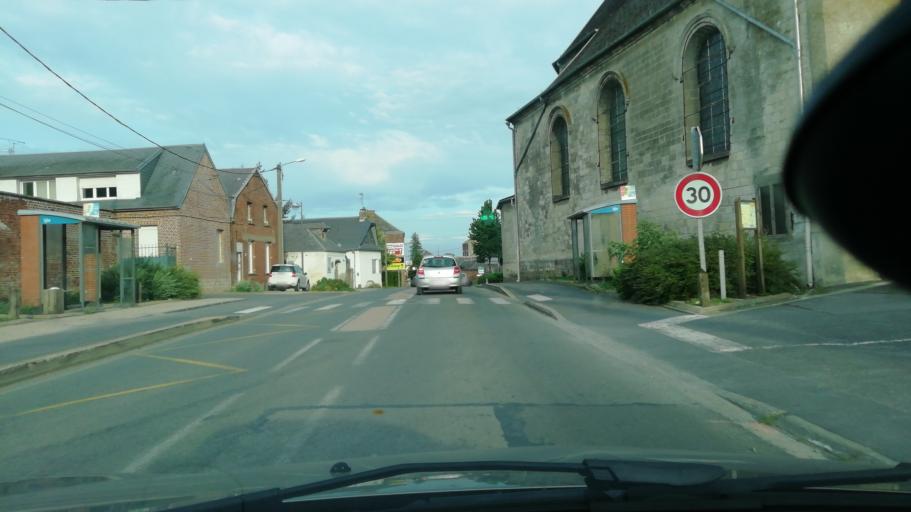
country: FR
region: Nord-Pas-de-Calais
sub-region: Departement du Nord
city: Viesly
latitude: 50.1228
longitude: 3.4614
